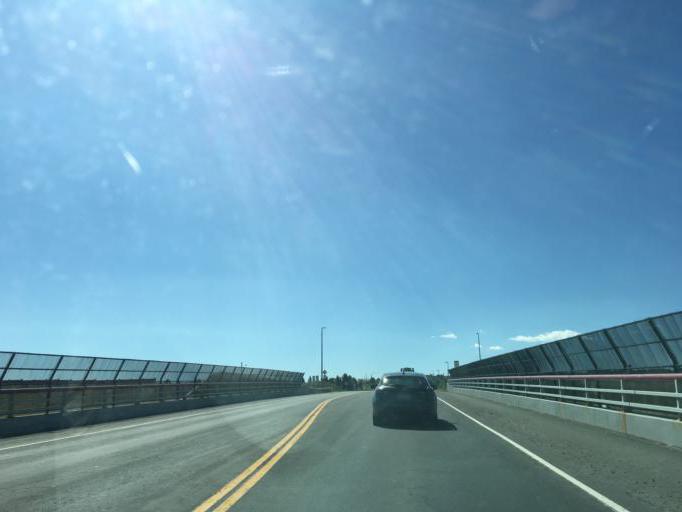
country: US
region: Colorado
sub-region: Douglas County
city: Parker
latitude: 39.5782
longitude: -104.7243
